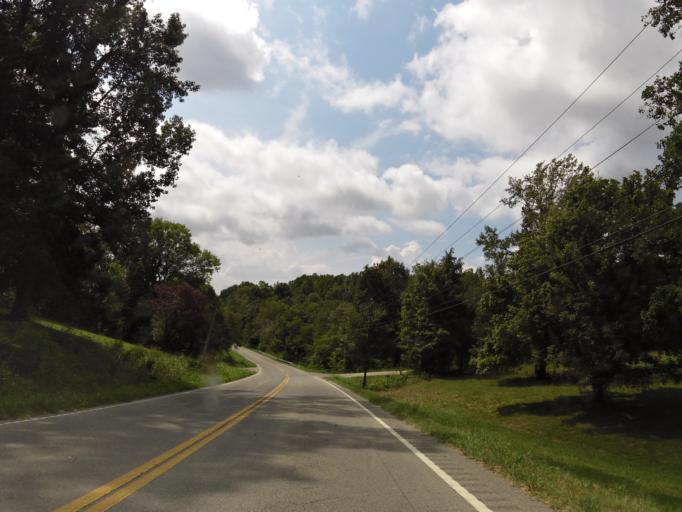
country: US
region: Tennessee
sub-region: Perry County
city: Linden
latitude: 35.6510
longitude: -87.8236
